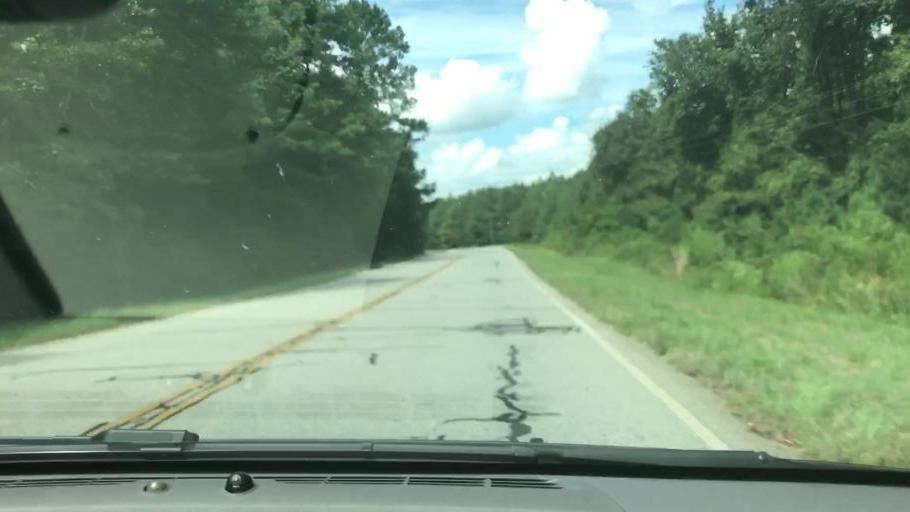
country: US
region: Georgia
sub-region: Stewart County
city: Lumpkin
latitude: 32.1487
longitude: -84.9003
